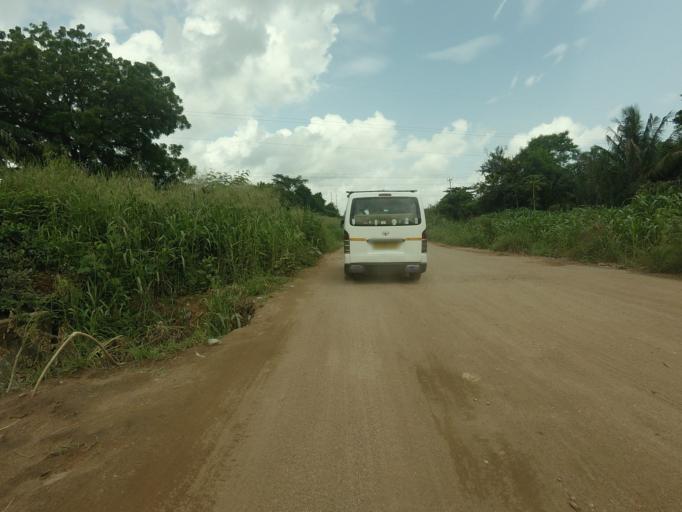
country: GH
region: Volta
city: Ho
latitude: 6.6924
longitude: 0.3355
